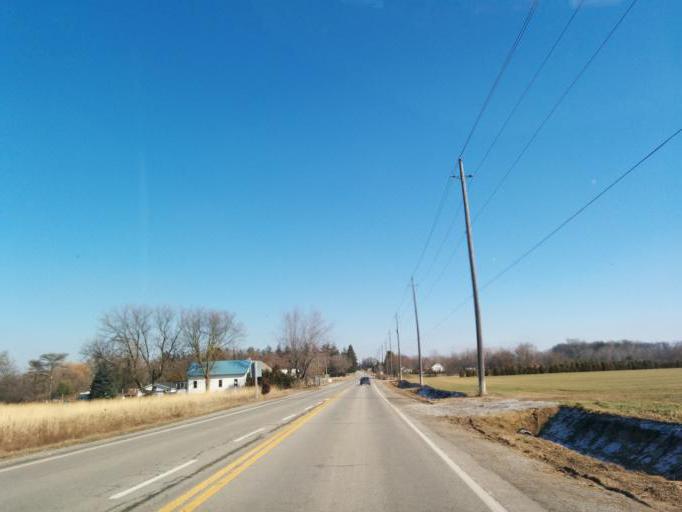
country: CA
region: Ontario
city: Norfolk County
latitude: 42.8299
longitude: -80.3339
